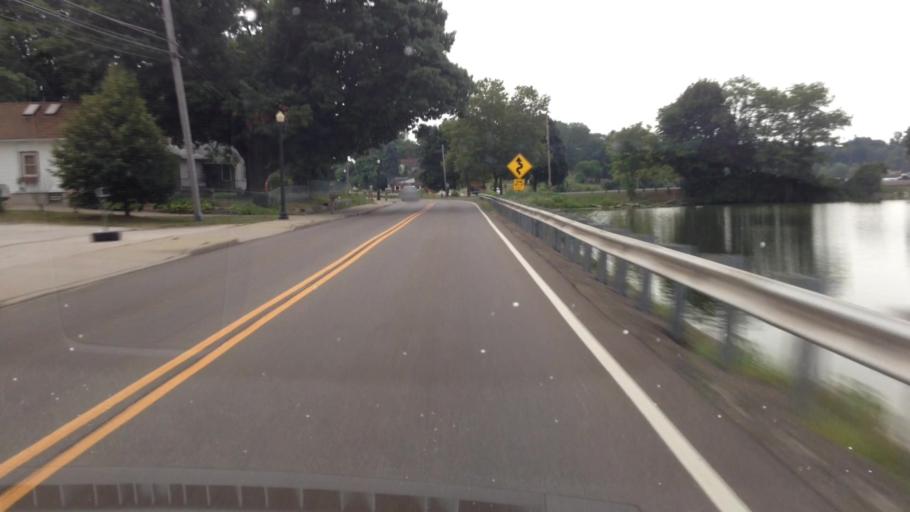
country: US
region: Ohio
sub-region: Summit County
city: Portage Lakes
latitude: 41.0048
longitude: -81.5479
